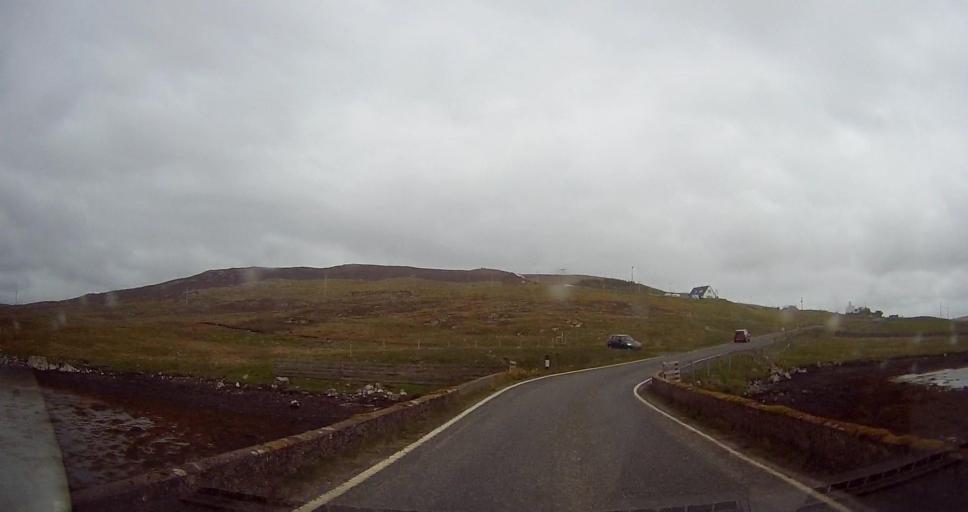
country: GB
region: Scotland
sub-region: Shetland Islands
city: Sandwick
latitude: 60.2446
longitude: -1.5303
